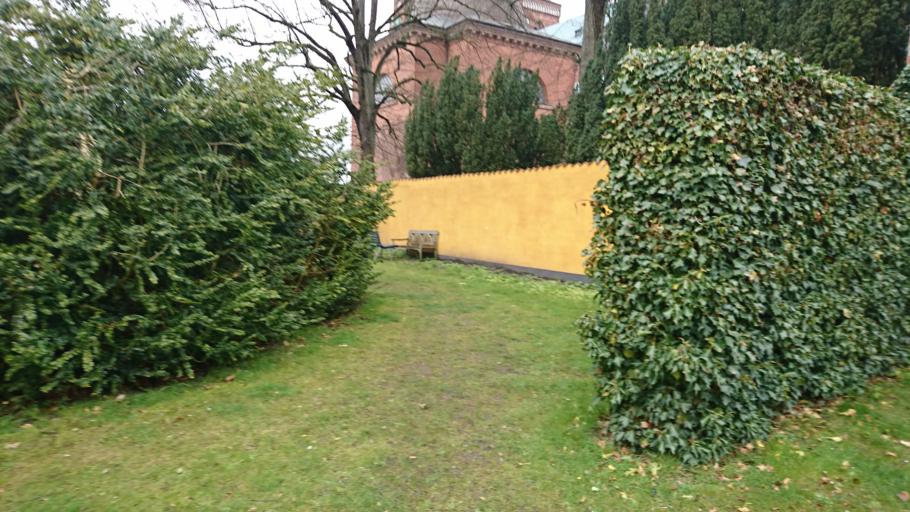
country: DK
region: Zealand
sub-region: Roskilde Kommune
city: Roskilde
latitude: 55.6421
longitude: 12.0810
